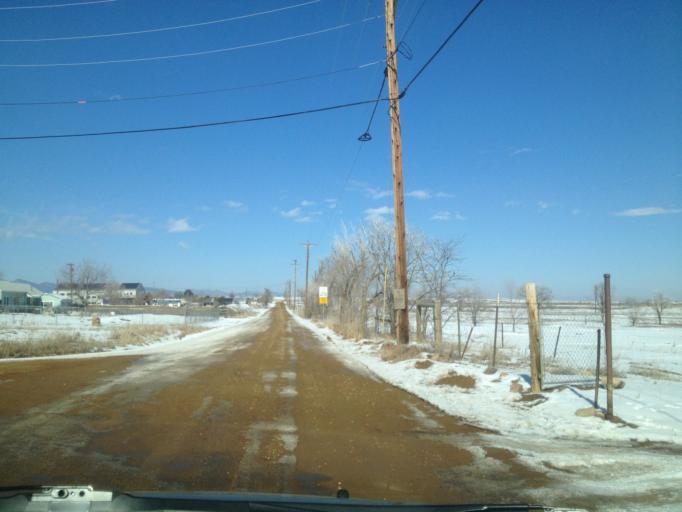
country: US
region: Colorado
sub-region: Boulder County
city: Boulder
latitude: 40.0582
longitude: -105.2634
